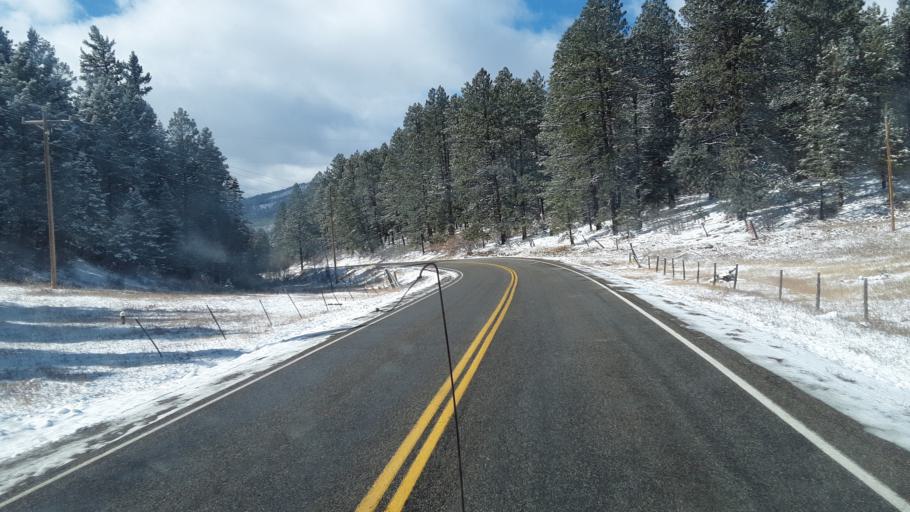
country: US
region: Colorado
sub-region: La Plata County
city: Bayfield
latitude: 37.3578
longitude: -107.6634
